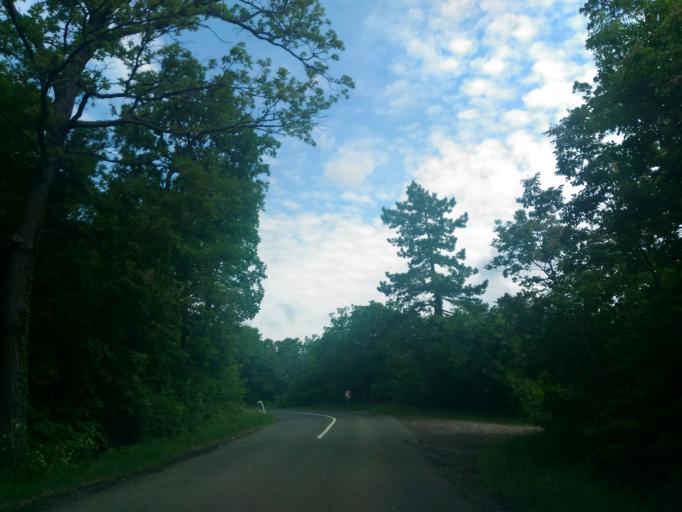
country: HU
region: Baranya
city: Pecs
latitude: 46.1000
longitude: 18.2268
